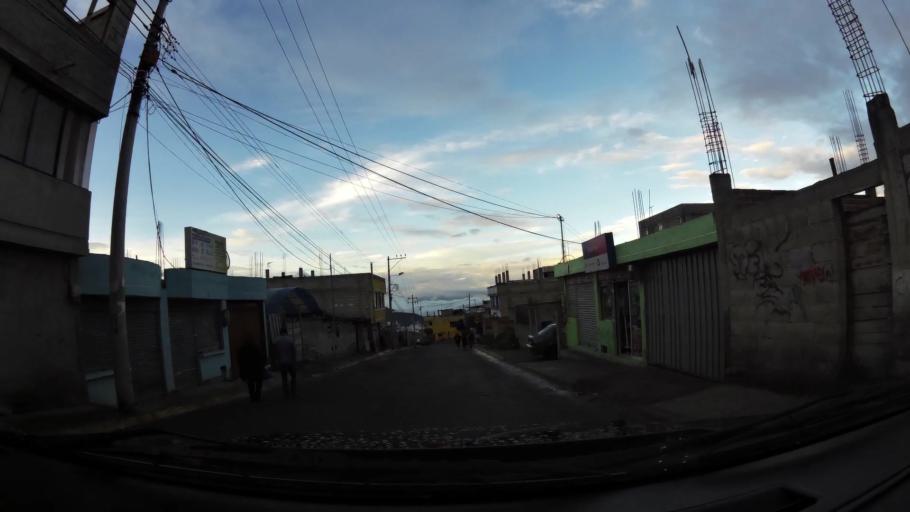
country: EC
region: Pichincha
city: Quito
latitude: -0.1000
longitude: -78.5212
